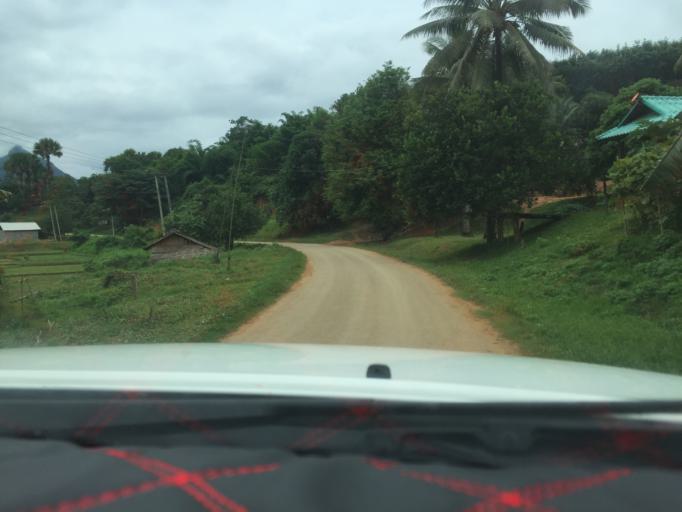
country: TH
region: Phayao
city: Phu Sang
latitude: 19.7697
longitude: 100.5461
